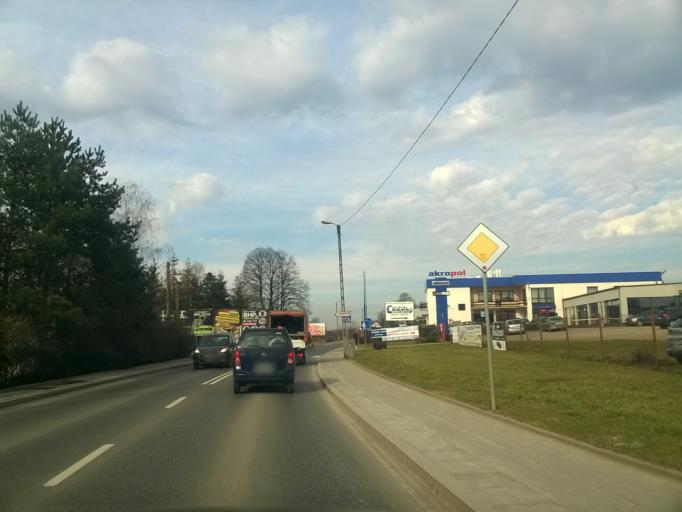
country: PL
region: Lesser Poland Voivodeship
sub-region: Powiat krakowski
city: Rzaska
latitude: 50.0808
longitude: 19.8716
